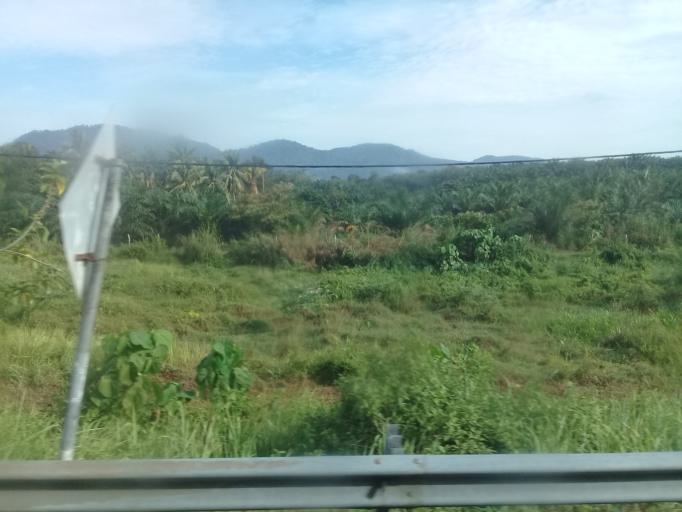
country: MY
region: Perak
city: Batu Gajah
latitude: 4.4795
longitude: 101.0019
